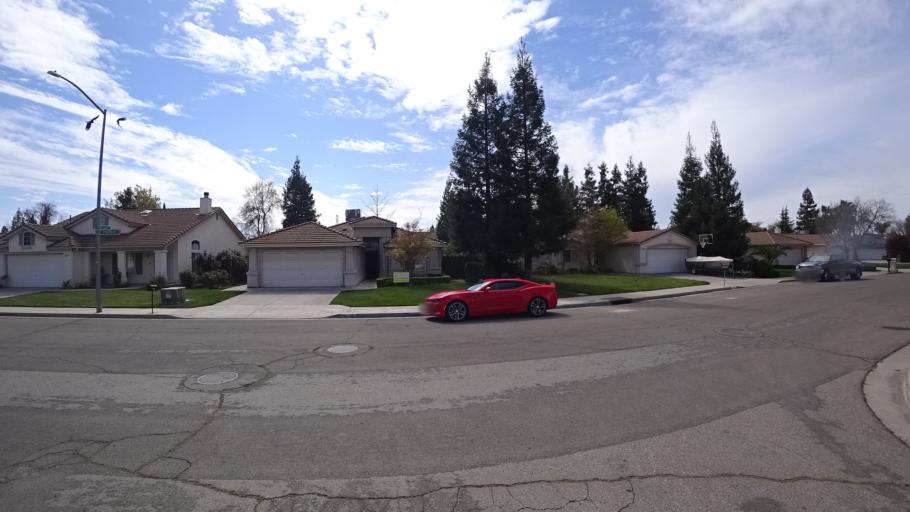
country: US
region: California
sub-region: Fresno County
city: Biola
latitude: 36.8432
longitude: -119.8919
